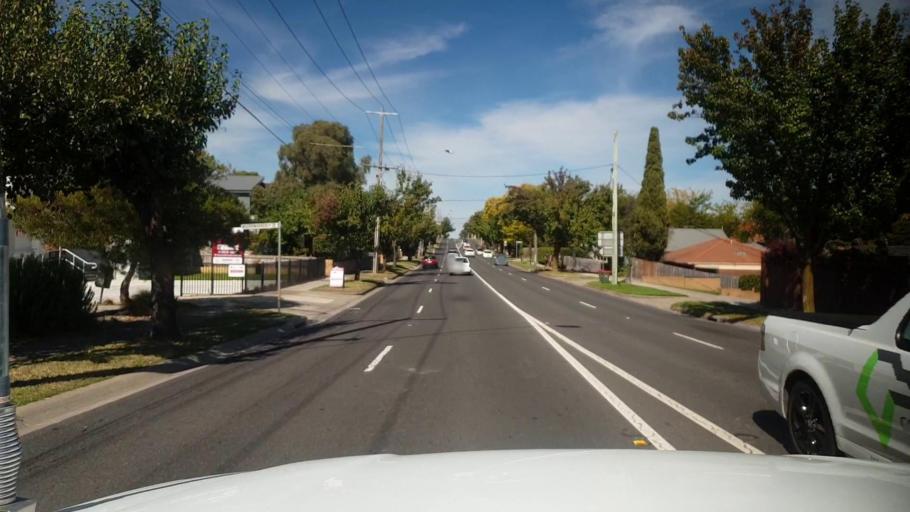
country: AU
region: Victoria
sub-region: Whitehorse
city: Blackburn North
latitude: -37.8098
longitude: 145.1405
